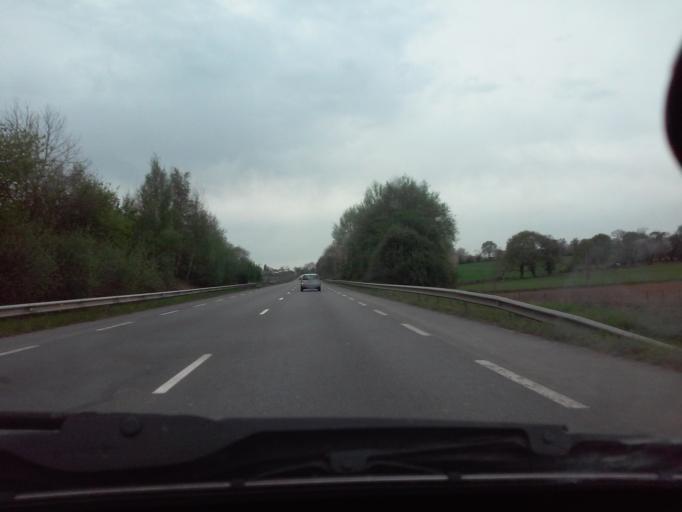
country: FR
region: Brittany
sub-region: Departement d'Ille-et-Vilaine
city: Fougeres
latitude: 48.3425
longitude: -1.2202
